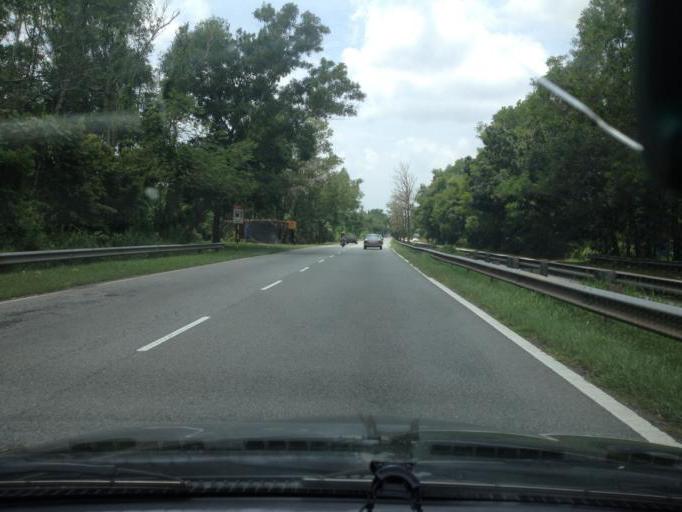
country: MY
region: Kedah
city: Sungai Petani
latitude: 5.6446
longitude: 100.5392
